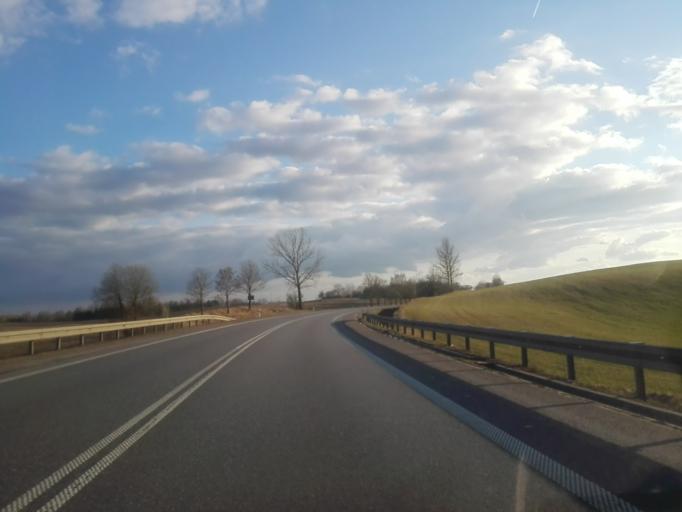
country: PL
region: Podlasie
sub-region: Suwalki
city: Suwalki
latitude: 54.1922
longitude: 23.0110
